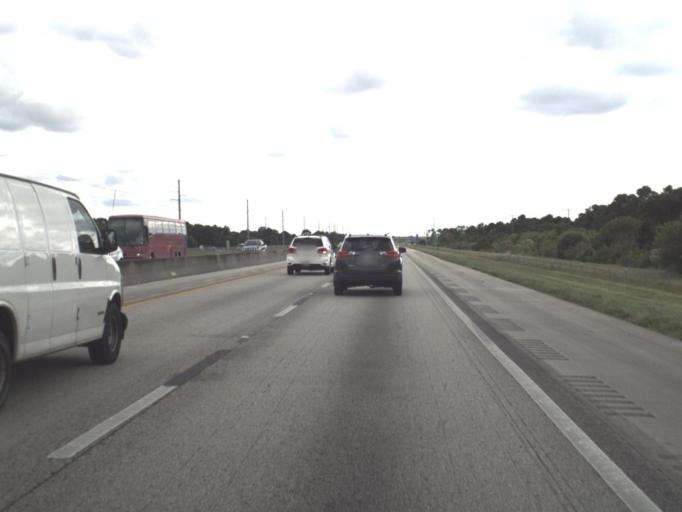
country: US
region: Florida
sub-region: Saint Lucie County
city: River Park
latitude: 27.3287
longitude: -80.3744
